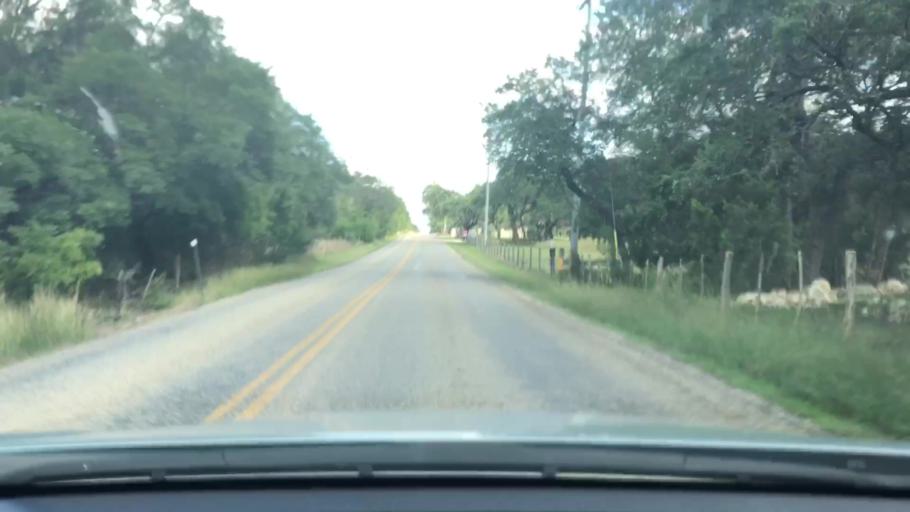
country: US
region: Texas
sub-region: Bexar County
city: Fair Oaks Ranch
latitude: 29.7854
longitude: -98.6428
